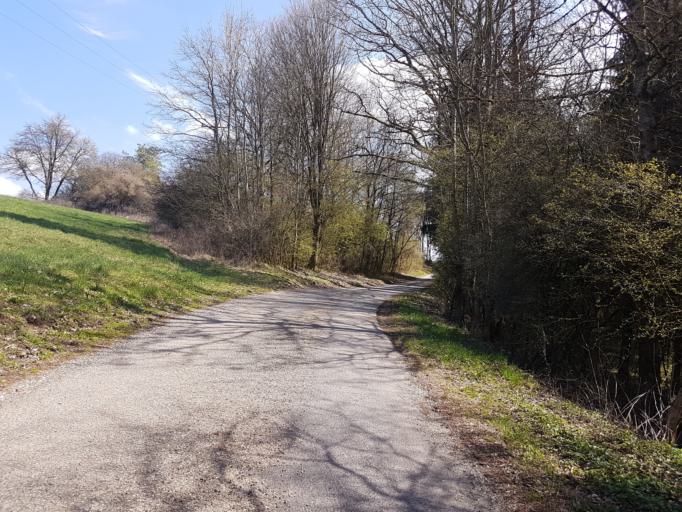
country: DE
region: Baden-Wuerttemberg
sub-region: Karlsruhe Region
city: Rosenberg
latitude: 49.3884
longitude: 9.5045
